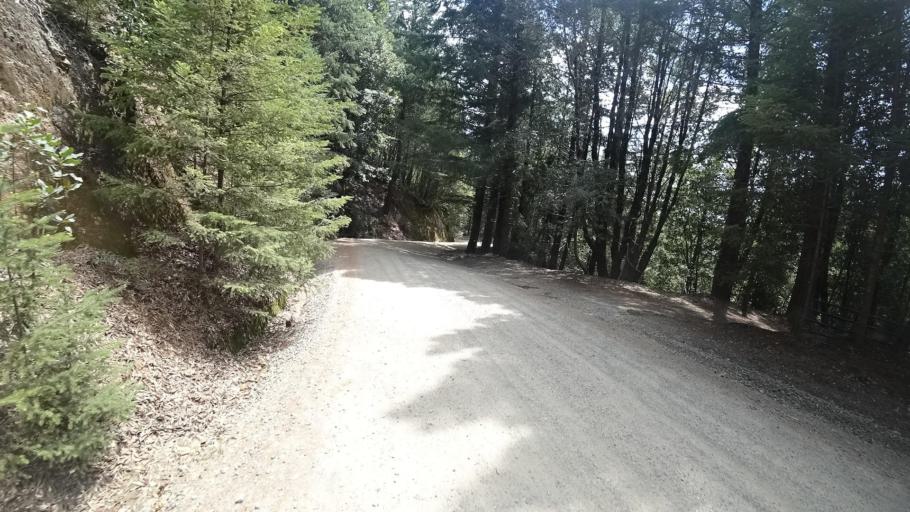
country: US
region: California
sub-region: Humboldt County
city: Redway
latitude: 40.0122
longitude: -123.9861
